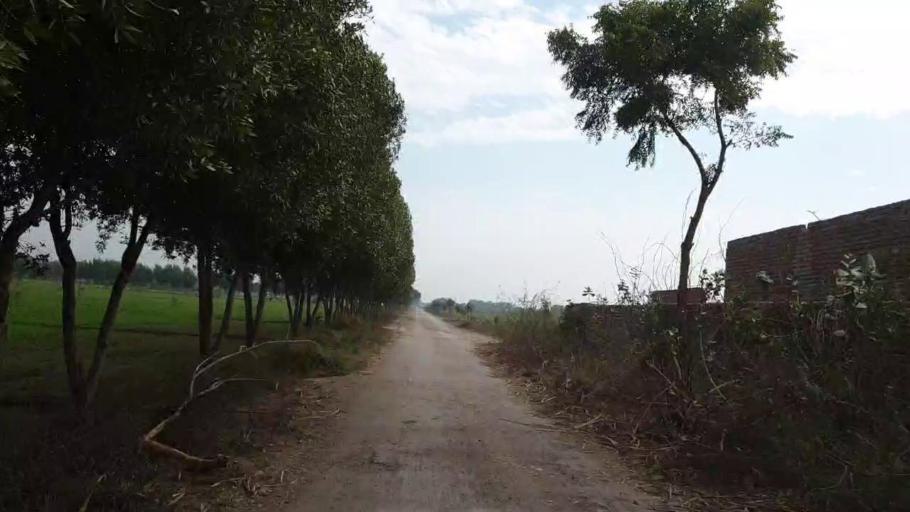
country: PK
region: Sindh
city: Matiari
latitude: 25.5795
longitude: 68.4434
